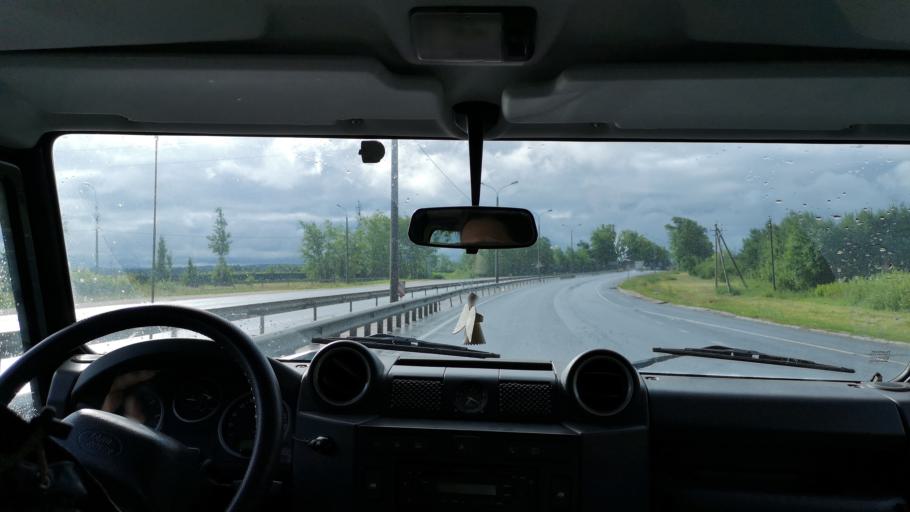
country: RU
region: Moskovskaya
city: Dmitrov
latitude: 56.3644
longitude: 37.4772
